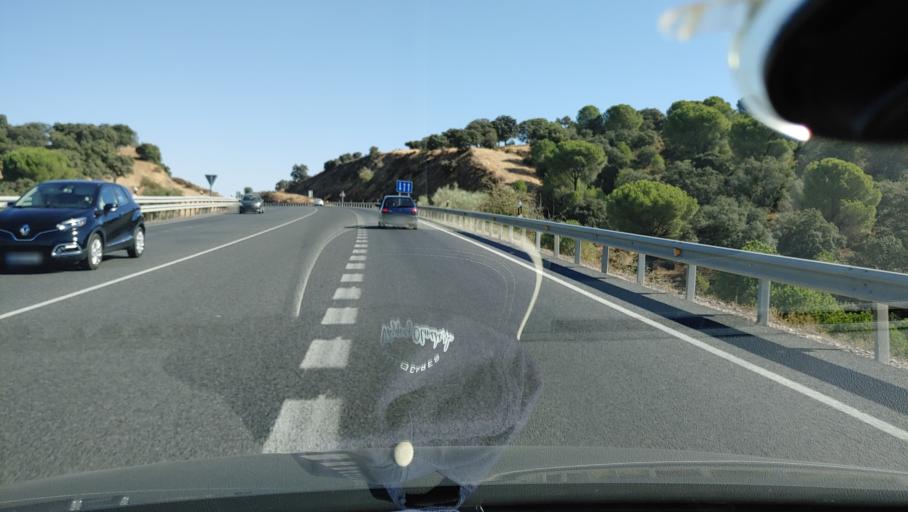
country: ES
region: Andalusia
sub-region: Province of Cordoba
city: Cordoba
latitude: 37.9873
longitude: -4.7862
